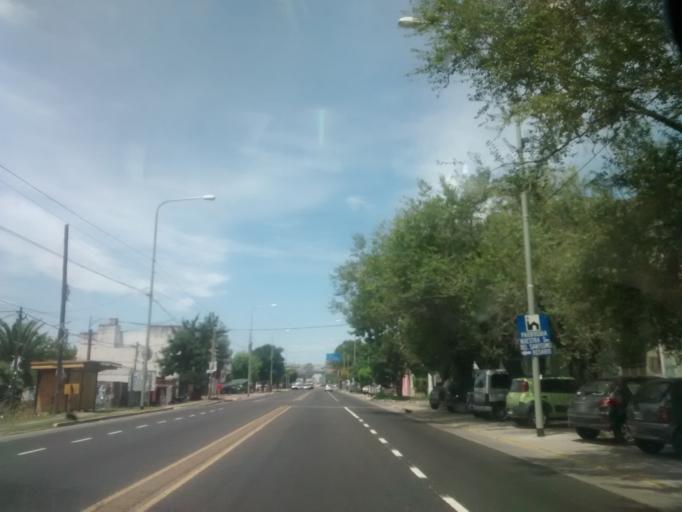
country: AR
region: Buenos Aires
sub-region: Partido de La Plata
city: La Plata
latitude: -34.9002
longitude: -57.9365
